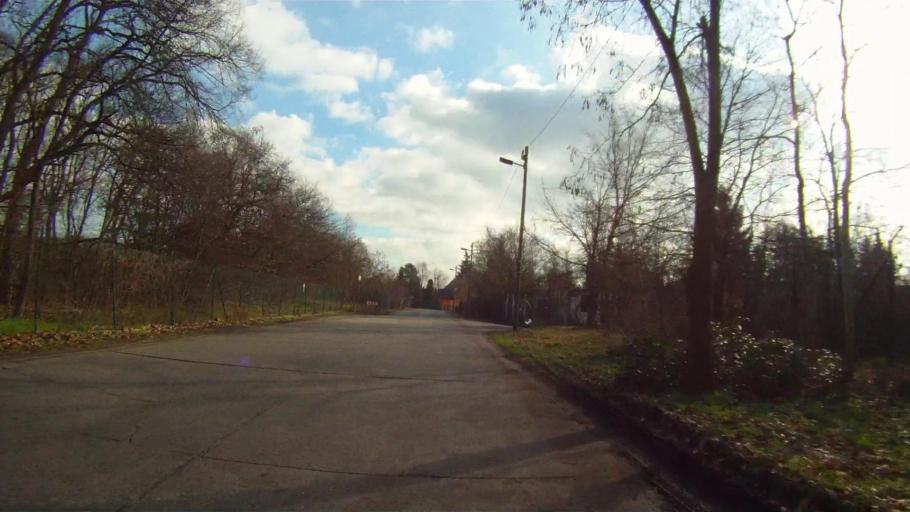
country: DE
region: Berlin
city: Kaulsdorf
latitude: 52.4901
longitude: 13.5787
